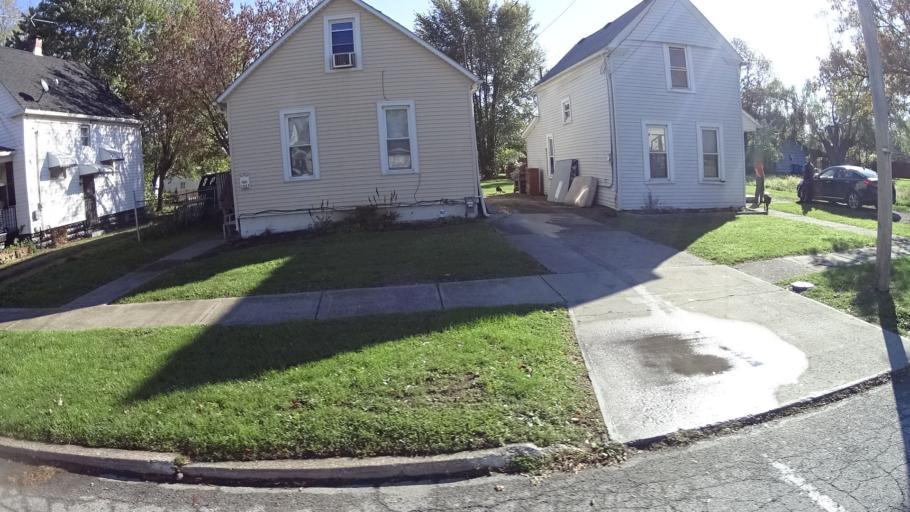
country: US
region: Ohio
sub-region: Lorain County
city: Lorain
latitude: 41.4381
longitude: -82.1572
